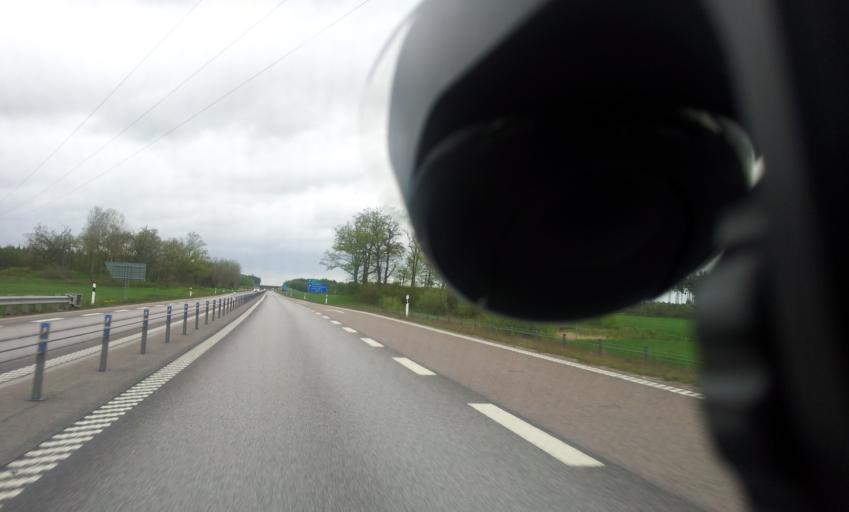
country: SE
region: Kalmar
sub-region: Kalmar Kommun
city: Ljungbyholm
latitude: 56.5830
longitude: 16.1172
